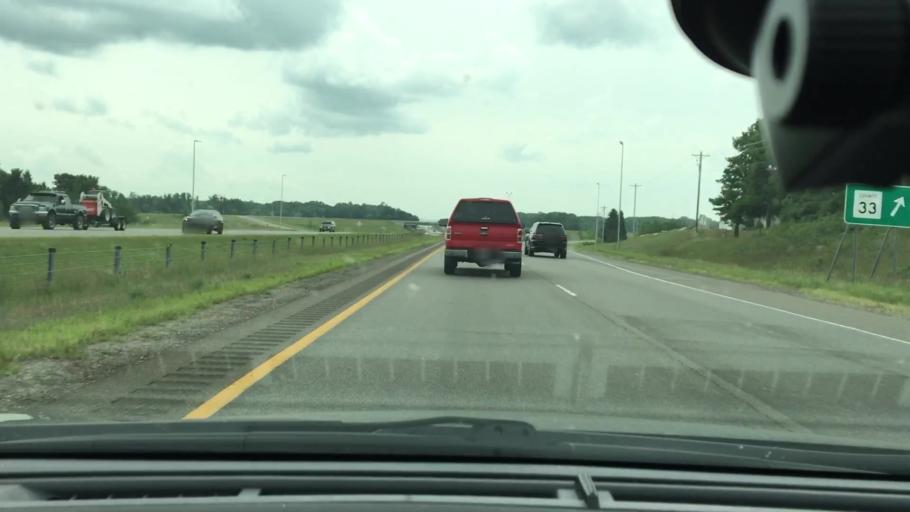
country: US
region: Minnesota
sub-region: Sherburne County
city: Elk River
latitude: 45.3481
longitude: -93.5586
